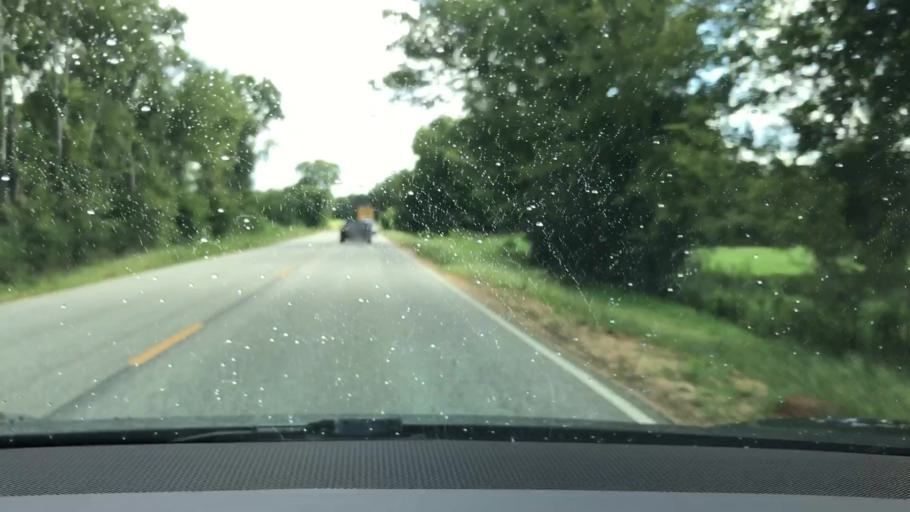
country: US
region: Alabama
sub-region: Montgomery County
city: Pike Road
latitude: 32.2364
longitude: -86.0932
